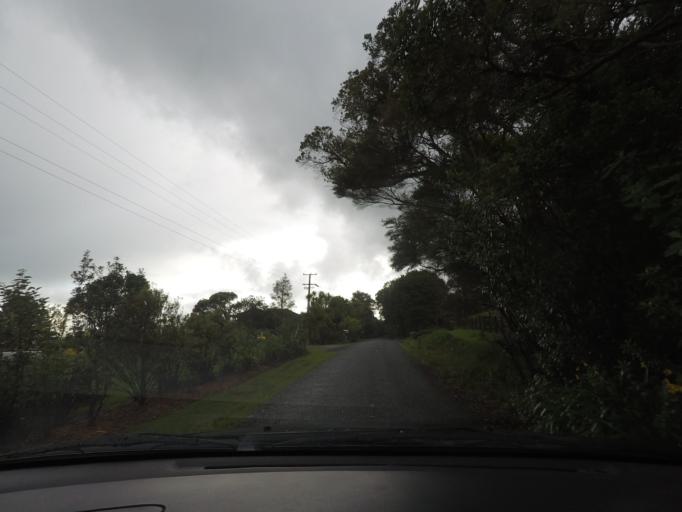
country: NZ
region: Auckland
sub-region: Auckland
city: Warkworth
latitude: -36.4753
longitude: 174.7351
